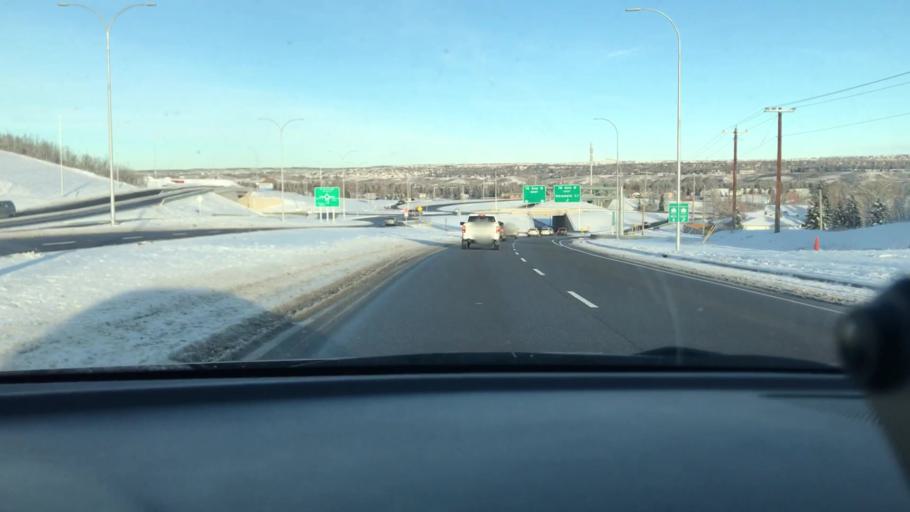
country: CA
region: Alberta
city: Calgary
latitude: 51.0759
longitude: -114.1870
